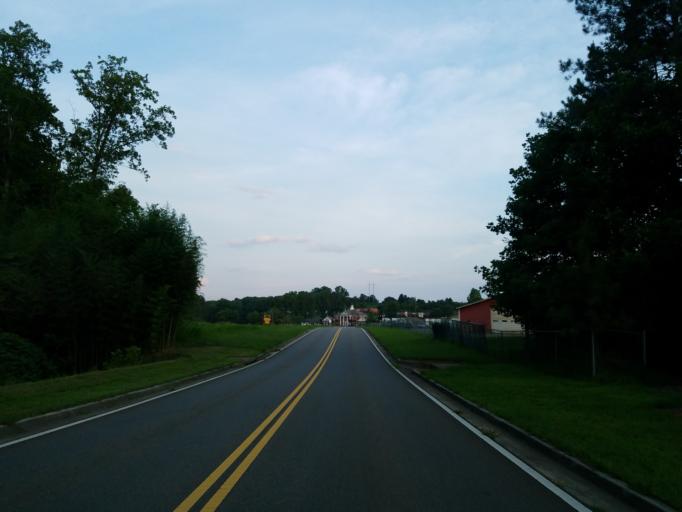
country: US
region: Georgia
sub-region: Pickens County
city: Jasper
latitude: 34.4681
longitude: -84.4519
